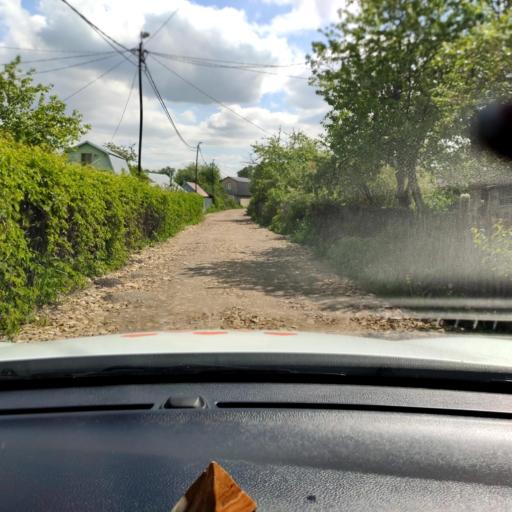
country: RU
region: Tatarstan
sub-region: Gorod Kazan'
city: Kazan
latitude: 55.8599
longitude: 49.1888
